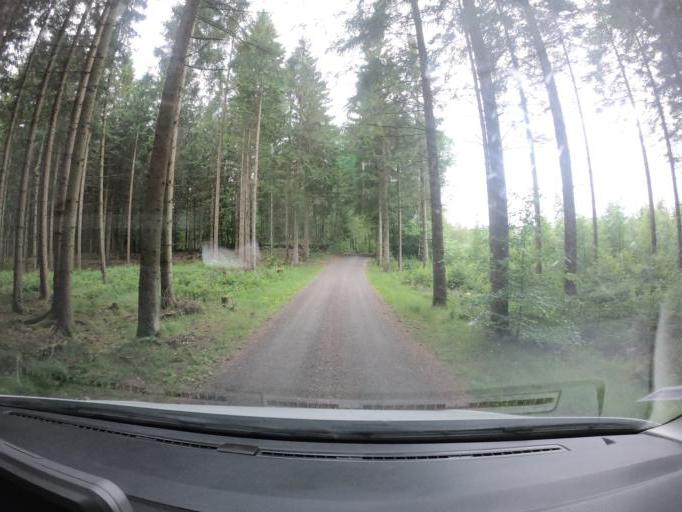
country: SE
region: Skane
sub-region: Hassleholms Kommun
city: Sosdala
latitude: 56.1006
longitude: 13.5523
